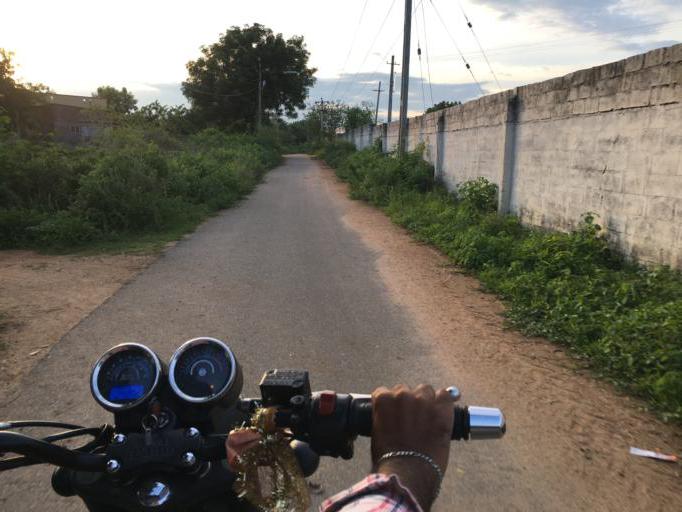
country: IN
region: Telangana
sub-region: Nalgonda
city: Nalgonda
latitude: 17.1746
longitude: 79.4172
